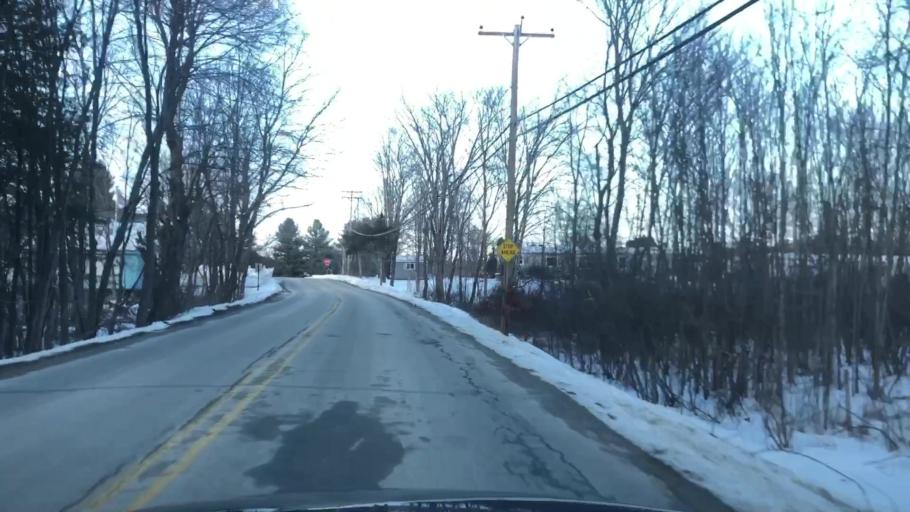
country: US
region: New Hampshire
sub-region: Hillsborough County
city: Milford
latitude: 42.8175
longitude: -71.6656
